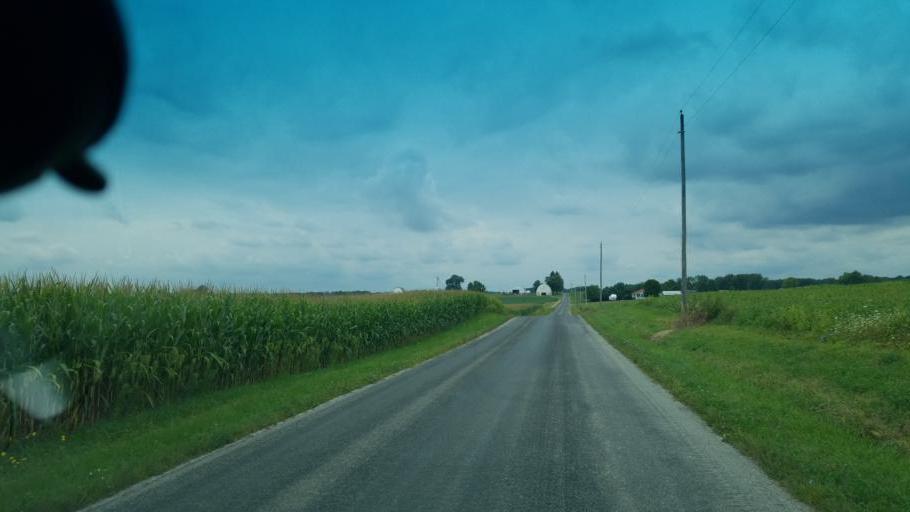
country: US
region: Ohio
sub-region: Richland County
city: Shelby
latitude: 40.9383
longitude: -82.5727
